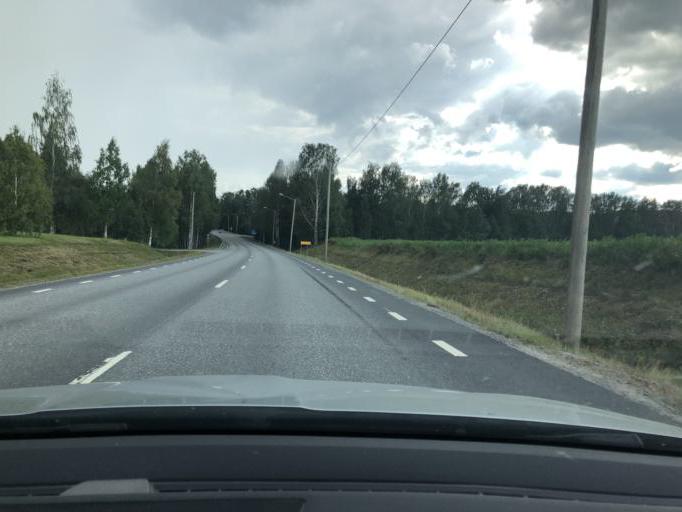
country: SE
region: Vaesternorrland
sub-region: Solleftea Kommun
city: Solleftea
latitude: 63.2435
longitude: 17.2073
